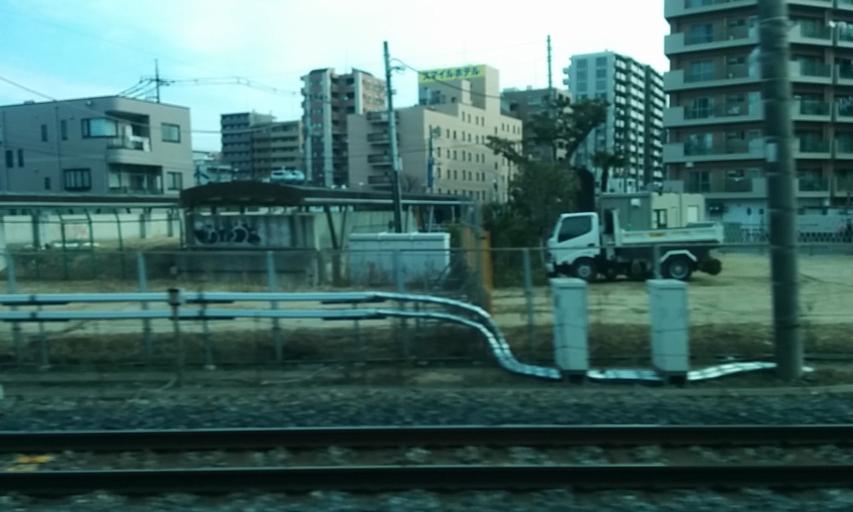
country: JP
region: Saitama
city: Kawaguchi
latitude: 35.8043
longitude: 139.7157
